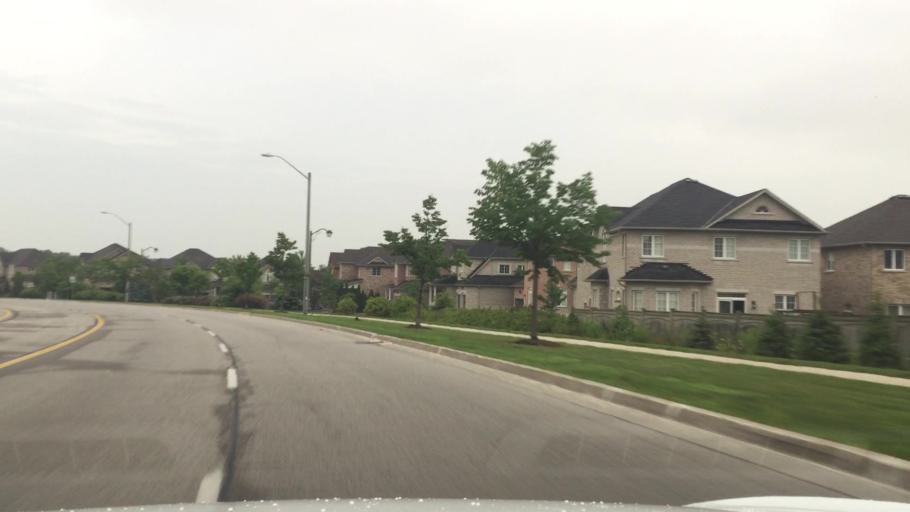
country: CA
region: Ontario
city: Markham
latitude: 43.8592
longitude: -79.2237
